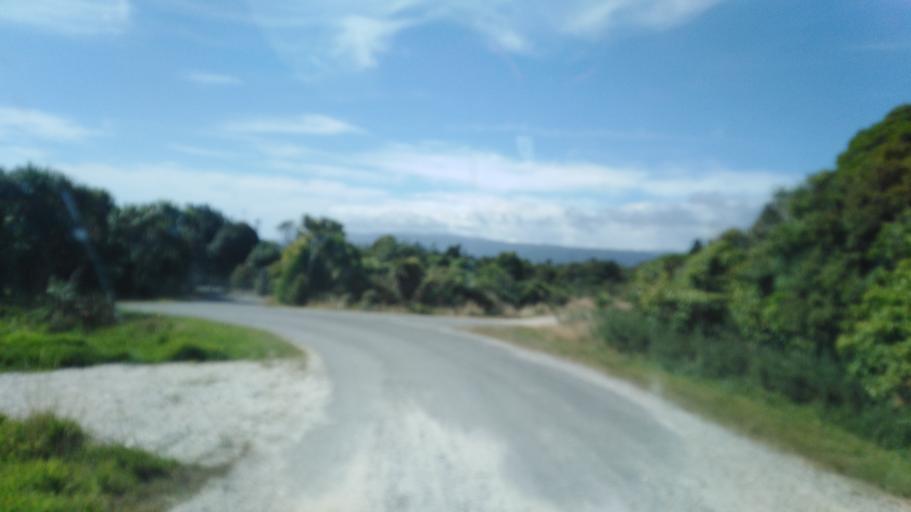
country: NZ
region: West Coast
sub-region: Buller District
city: Westport
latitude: -41.2622
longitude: 172.1145
